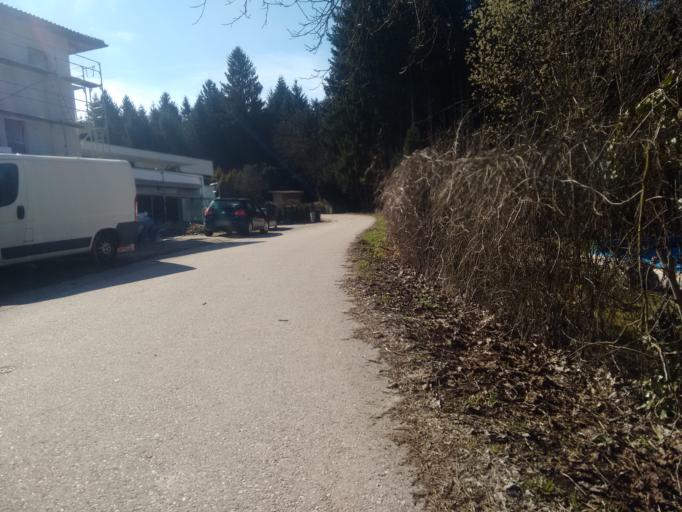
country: AT
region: Upper Austria
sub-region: Politischer Bezirk Grieskirchen
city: Bad Schallerbach
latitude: 48.2005
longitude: 13.9669
